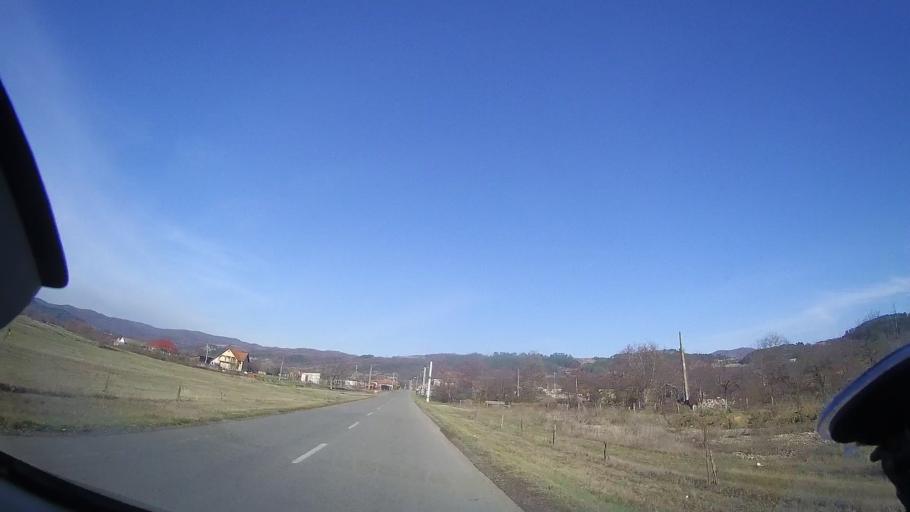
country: RO
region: Bihor
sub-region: Comuna Auseu
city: Auseu
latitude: 47.0301
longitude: 22.4929
